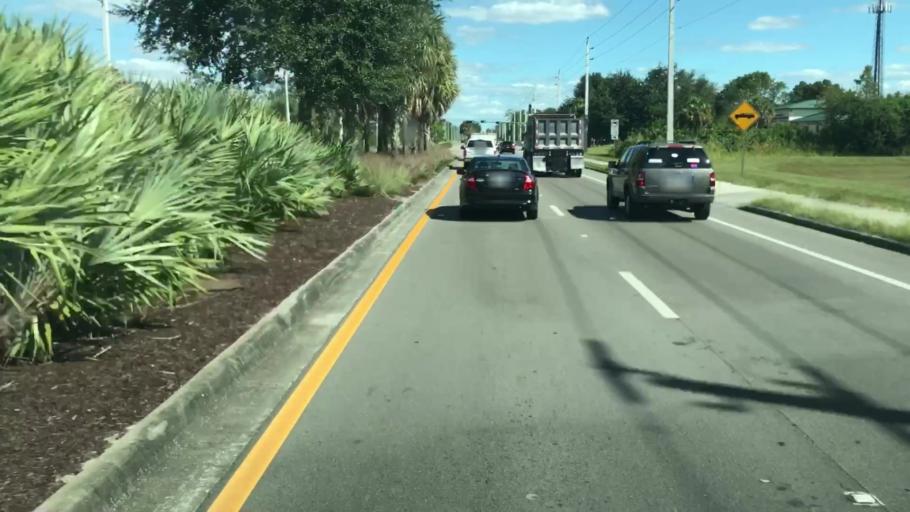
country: US
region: Florida
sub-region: Collier County
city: Golden Gate
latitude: 26.2295
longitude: -81.6348
